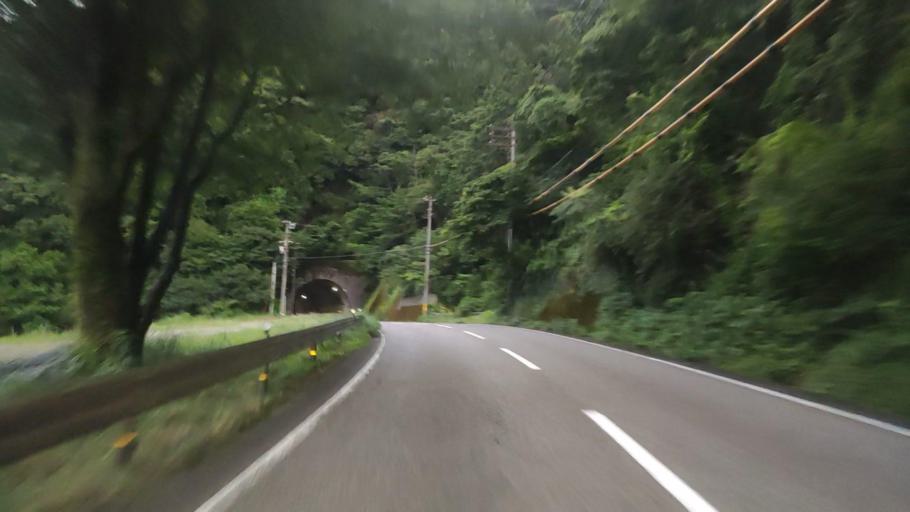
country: JP
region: Wakayama
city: Shingu
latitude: 33.7571
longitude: 135.9207
